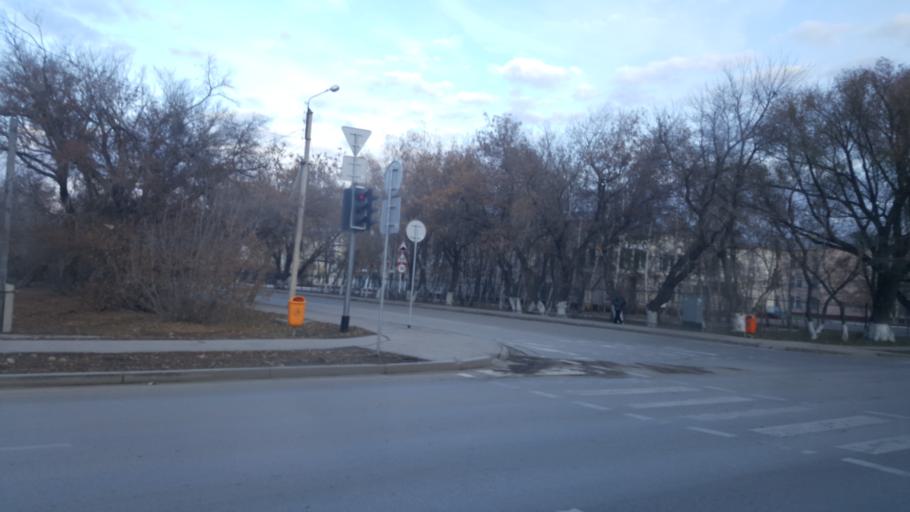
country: KZ
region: Astana Qalasy
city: Astana
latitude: 51.1654
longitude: 71.4546
